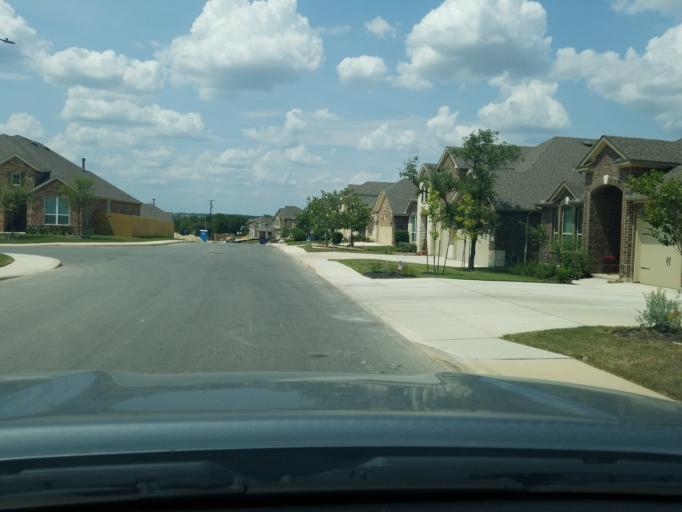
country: US
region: Texas
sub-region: Bexar County
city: Timberwood Park
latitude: 29.6831
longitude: -98.4788
